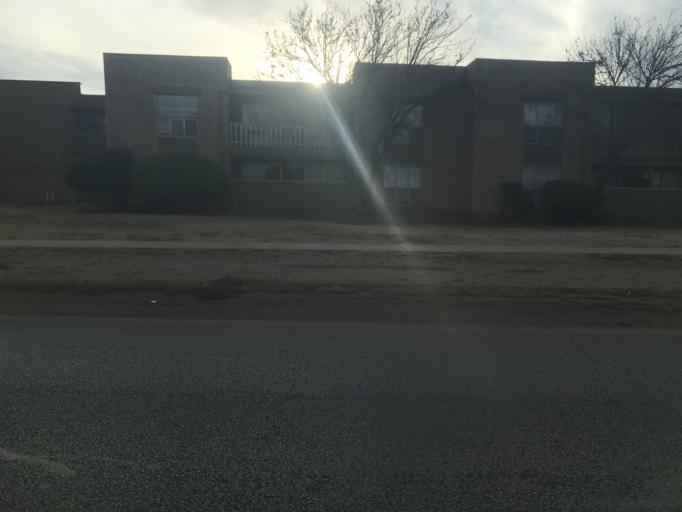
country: US
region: Texas
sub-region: Taylor County
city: Abilene
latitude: 32.4247
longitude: -99.7853
